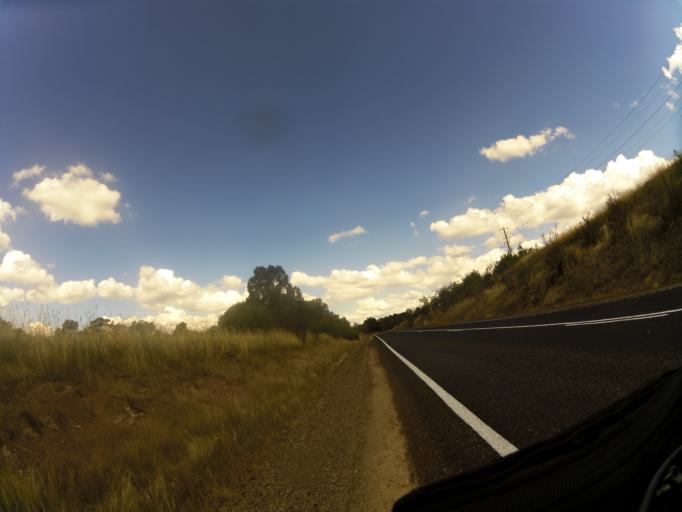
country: AU
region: Victoria
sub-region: Mansfield
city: Mansfield
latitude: -36.9074
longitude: 145.9980
